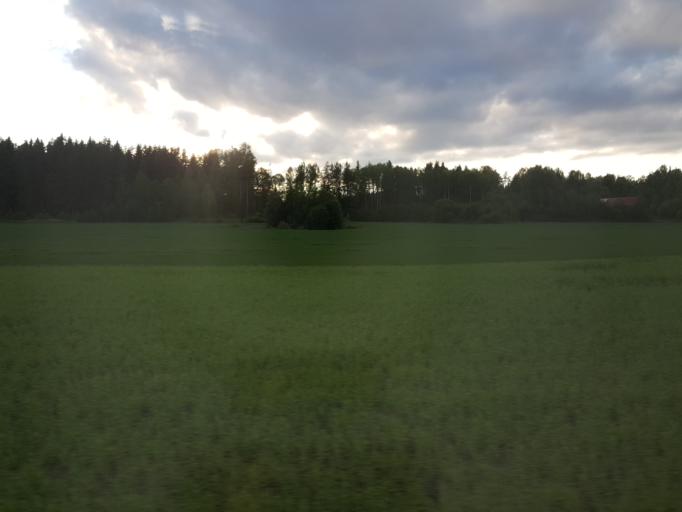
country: SE
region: Uppsala
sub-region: Osthammars Kommun
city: Gimo
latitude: 60.1549
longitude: 18.1866
